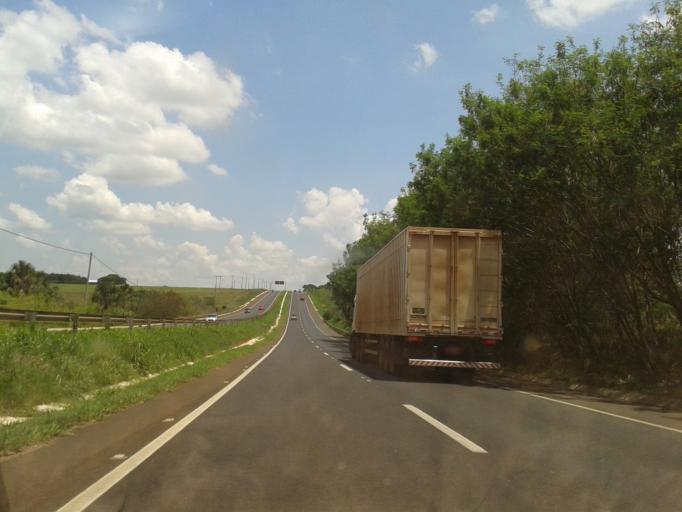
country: BR
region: Minas Gerais
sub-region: Uberlandia
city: Uberlandia
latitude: -18.8874
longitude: -48.4525
